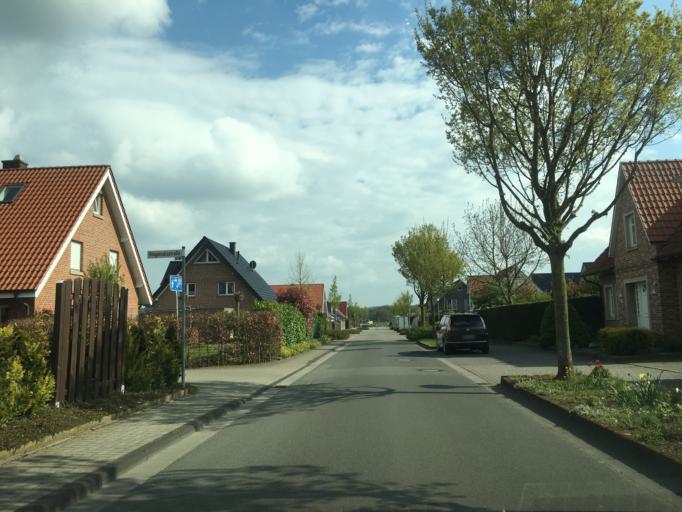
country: DE
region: North Rhine-Westphalia
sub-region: Regierungsbezirk Munster
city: Steinfurt
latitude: 52.1355
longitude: 7.3375
